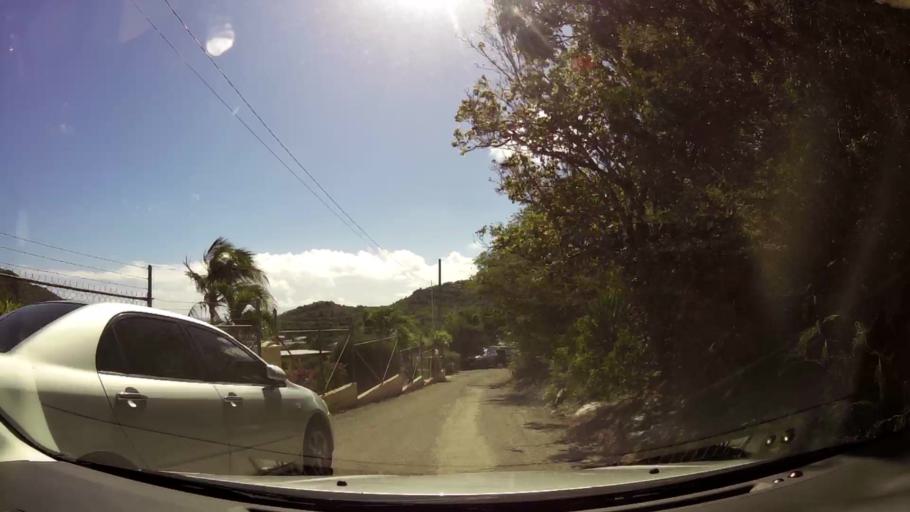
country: AG
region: Saint Paul
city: Falmouth
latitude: 17.0130
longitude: -61.7661
